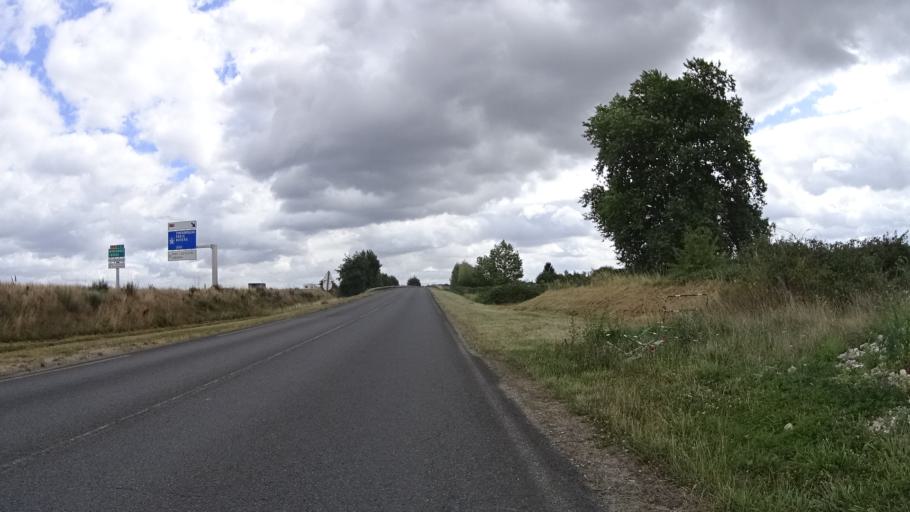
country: FR
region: Centre
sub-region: Departement du Loiret
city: Pannes
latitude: 47.9883
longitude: 2.6714
